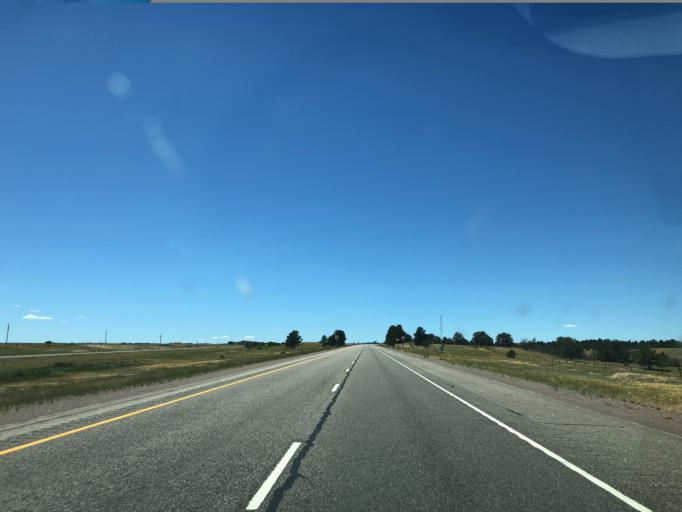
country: US
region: Wyoming
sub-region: Albany County
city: Laramie
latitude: 41.1261
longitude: -105.3182
